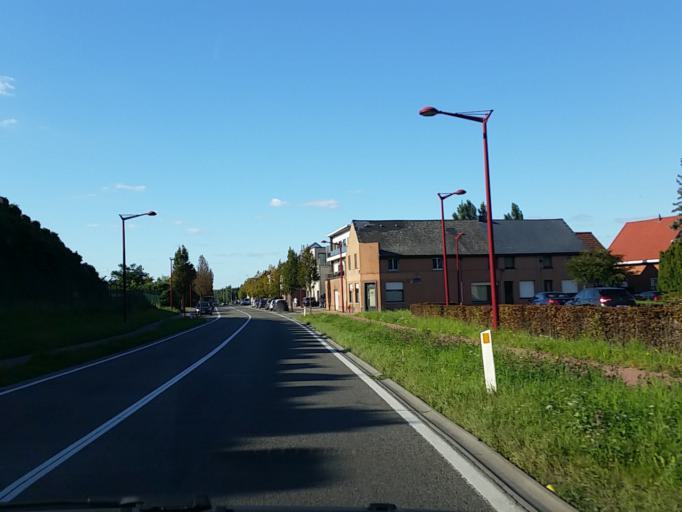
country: BE
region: Flanders
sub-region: Provincie Vlaams-Brabant
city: Steenokkerzeel
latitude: 50.9160
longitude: 4.5055
